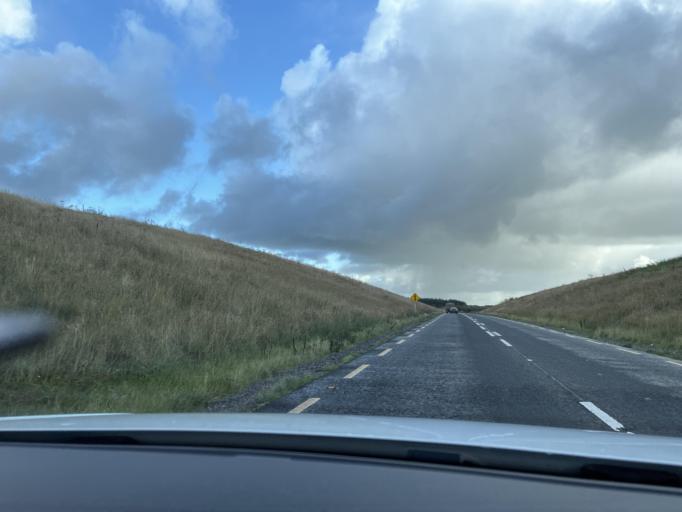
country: IE
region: Connaught
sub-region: Roscommon
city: Boyle
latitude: 53.8997
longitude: -8.2549
